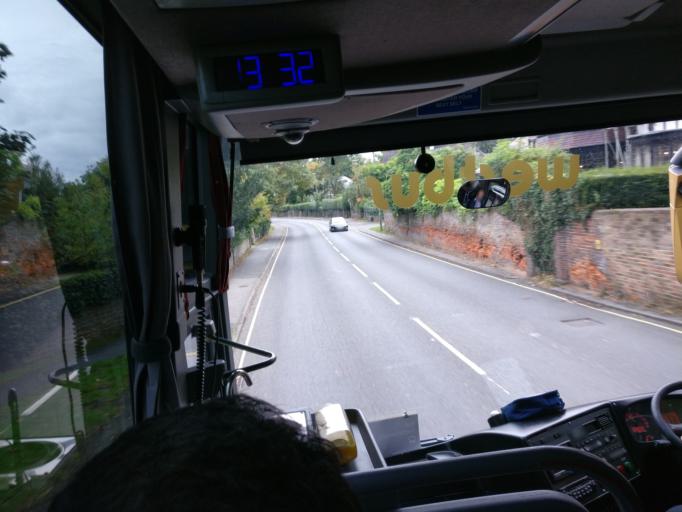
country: GB
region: England
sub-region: Surrey
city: Woking
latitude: 51.3276
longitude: -0.5622
